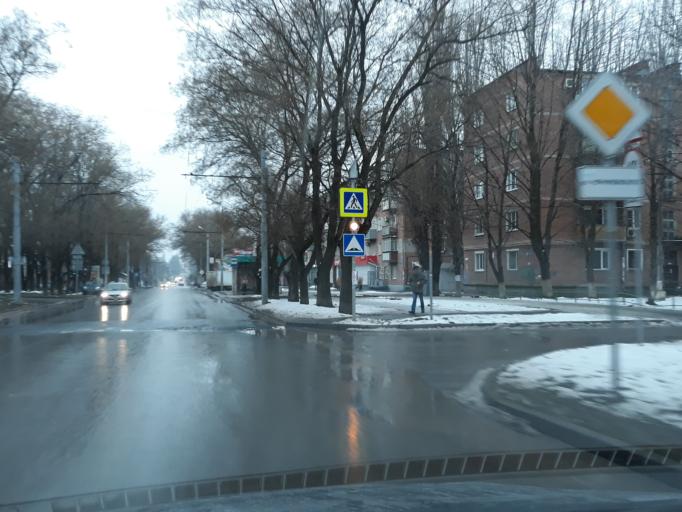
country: RU
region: Rostov
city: Taganrog
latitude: 47.2562
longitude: 38.9179
